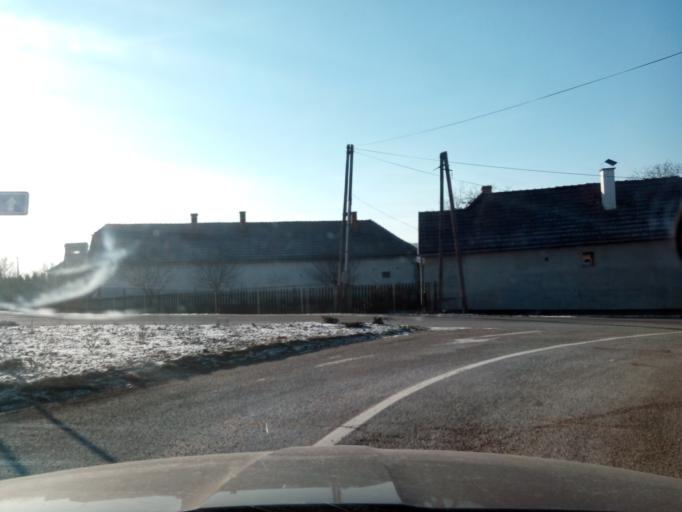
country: SK
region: Kosicky
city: Kosice
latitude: 48.6750
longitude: 21.1702
